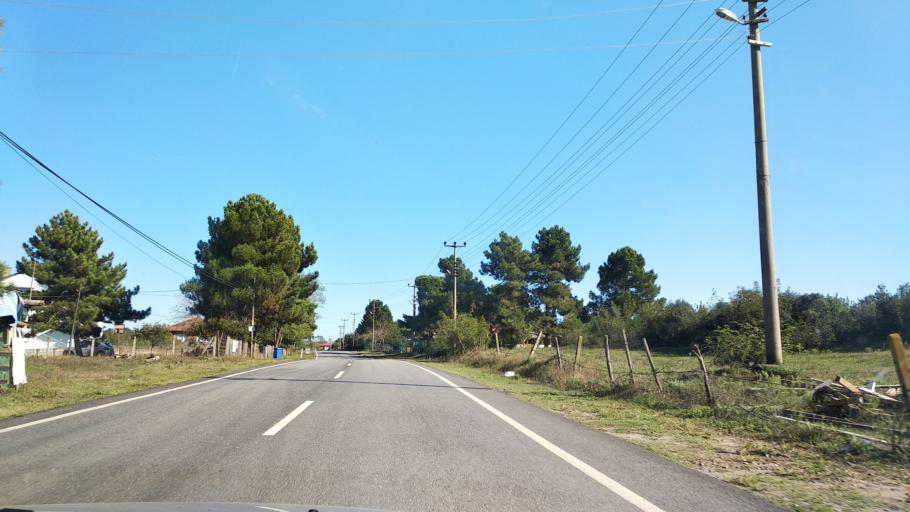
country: TR
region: Sakarya
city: Karasu
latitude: 41.1185
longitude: 30.6170
